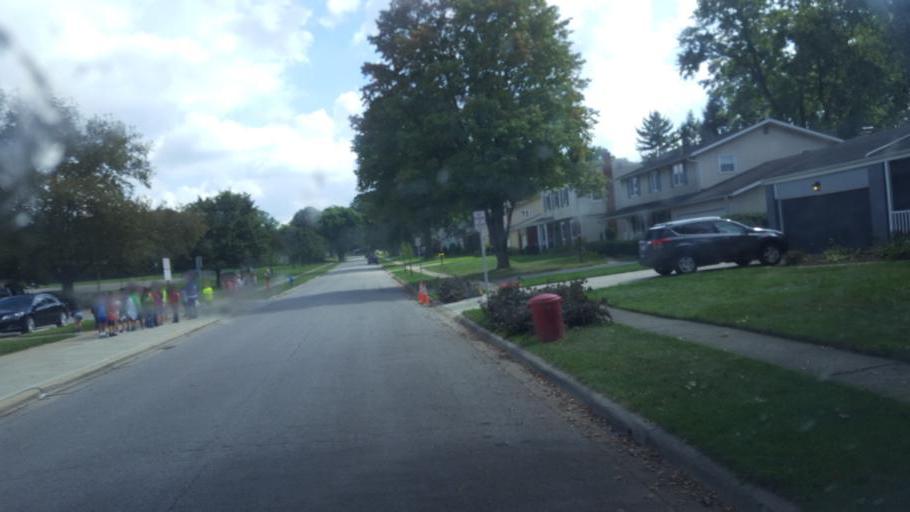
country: US
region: Ohio
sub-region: Franklin County
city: Worthington
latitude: 40.1018
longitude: -83.0278
